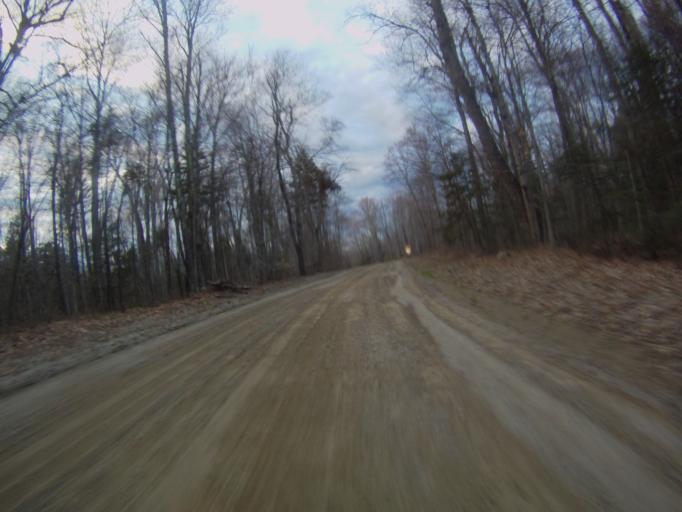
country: US
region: Vermont
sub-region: Rutland County
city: Brandon
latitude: 43.9386
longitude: -73.0218
